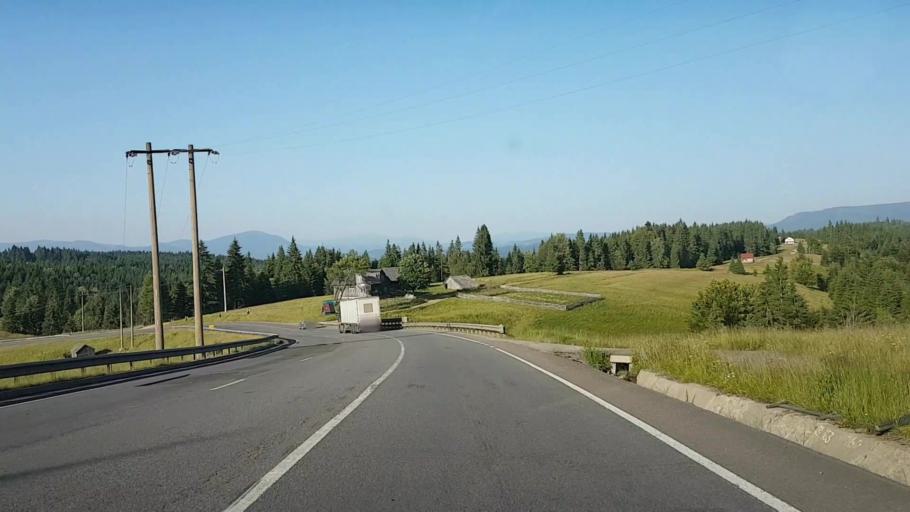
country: RO
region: Bistrita-Nasaud
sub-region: Comuna Lunca Ilvei
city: Lunca Ilvei
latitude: 47.2727
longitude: 25.0261
